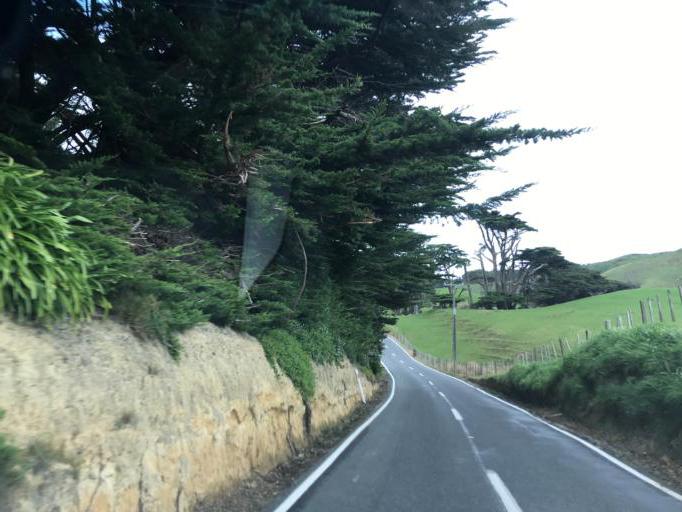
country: NZ
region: Wellington
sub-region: Porirua City
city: Porirua
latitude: -41.1937
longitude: 174.7841
